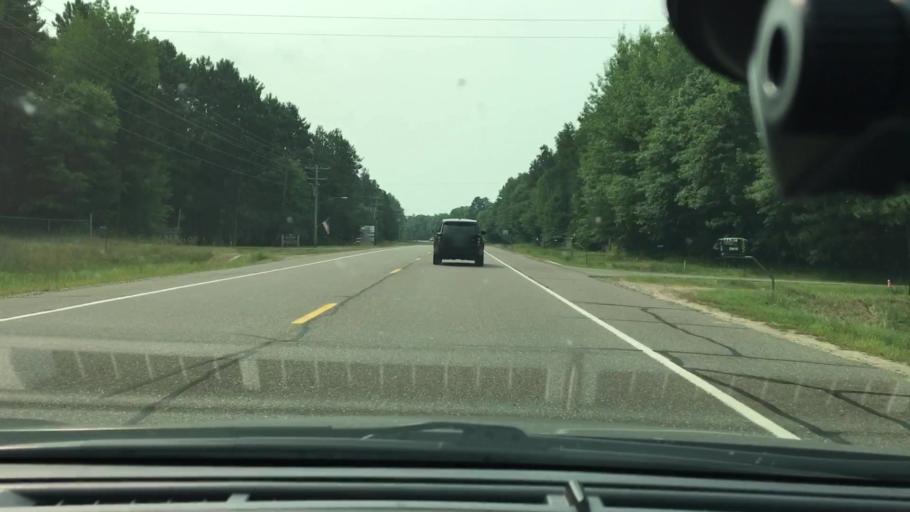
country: US
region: Minnesota
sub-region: Crow Wing County
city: Cross Lake
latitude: 46.5811
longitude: -94.1314
